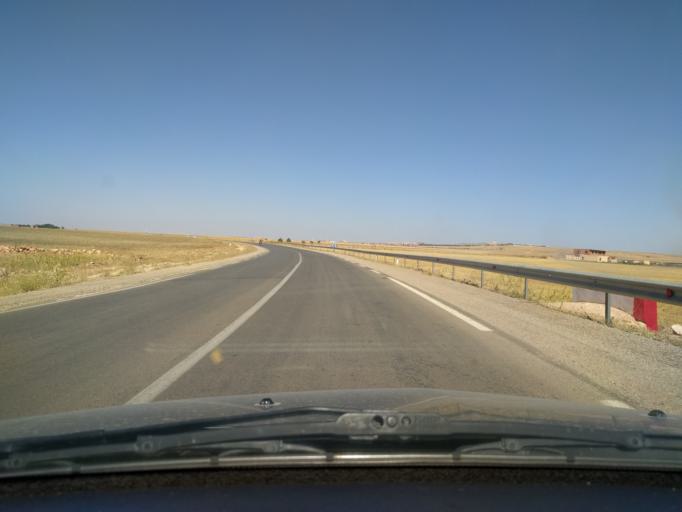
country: DZ
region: Tiaret
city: Frenda
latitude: 34.9051
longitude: 1.1443
